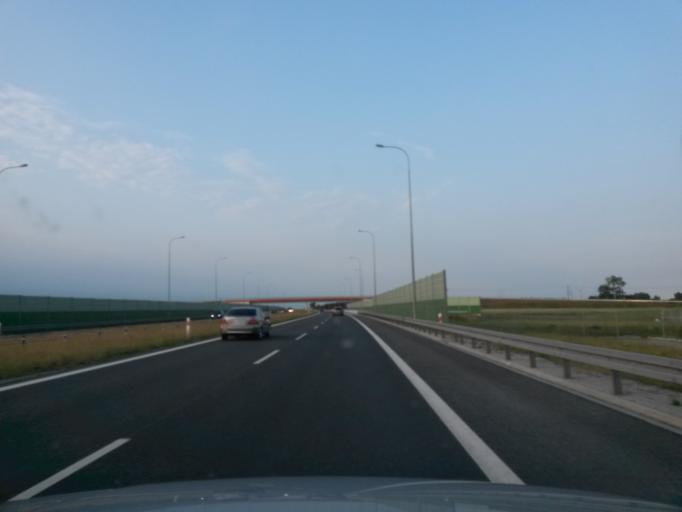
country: PL
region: Greater Poland Voivodeship
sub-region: Powiat kepinski
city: Slupia pod Kepnem
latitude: 51.3227
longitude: 18.0702
